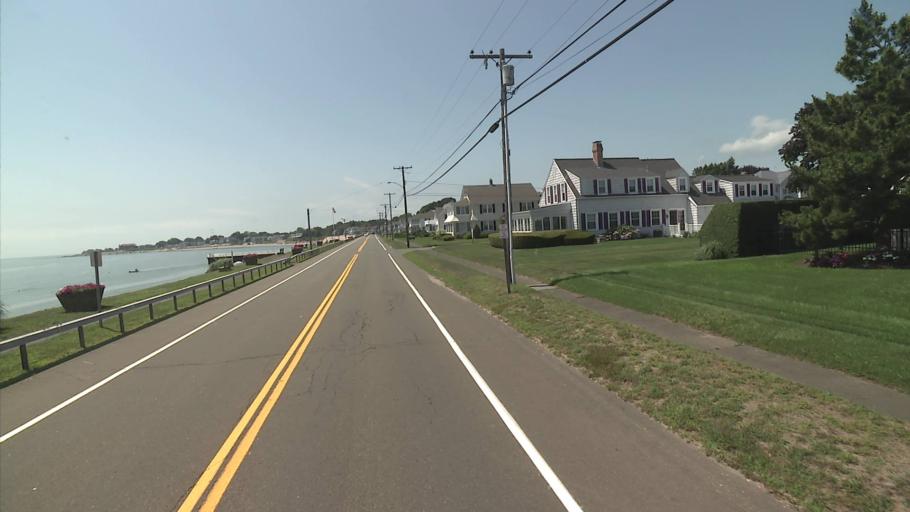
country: US
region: Connecticut
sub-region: Middlesex County
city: Old Saybrook
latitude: 41.2643
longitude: -72.3722
